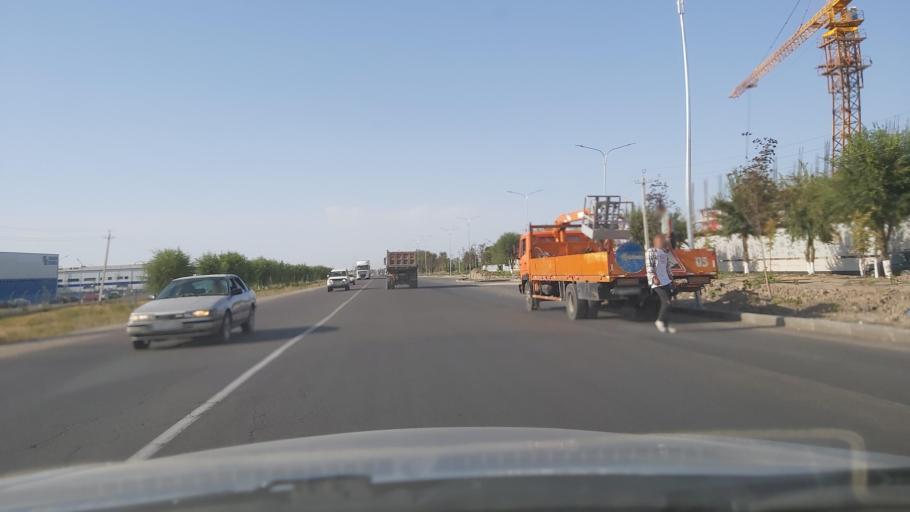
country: KZ
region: Almaty Oblysy
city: Energeticheskiy
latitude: 43.4599
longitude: 77.0337
